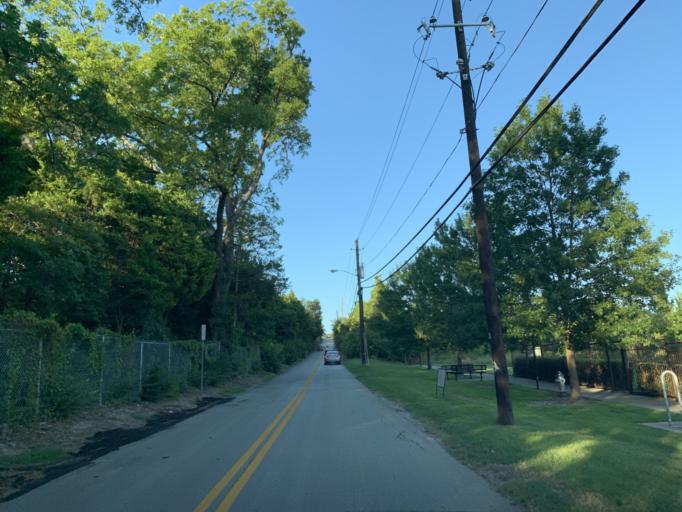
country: US
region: Texas
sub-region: Dallas County
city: Hutchins
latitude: 32.6707
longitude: -96.7876
